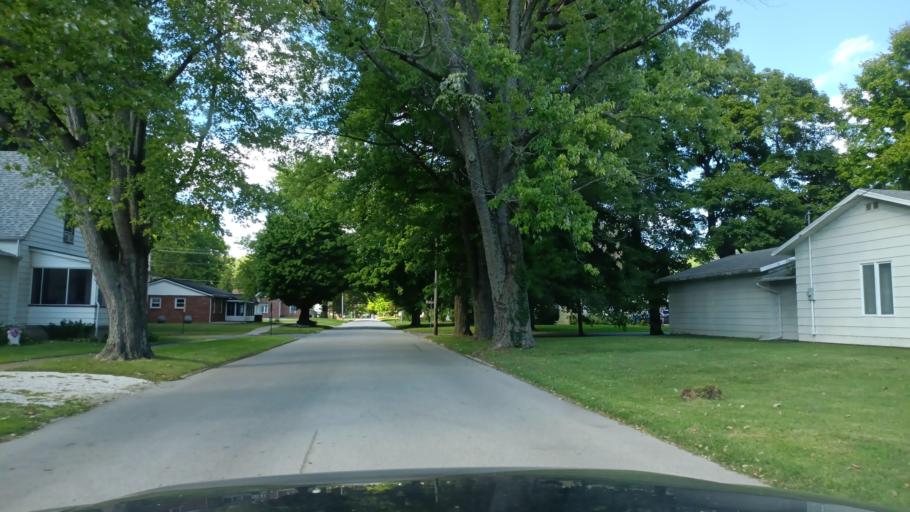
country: US
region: Indiana
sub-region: Fountain County
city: Covington
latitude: 40.1382
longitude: -87.3896
